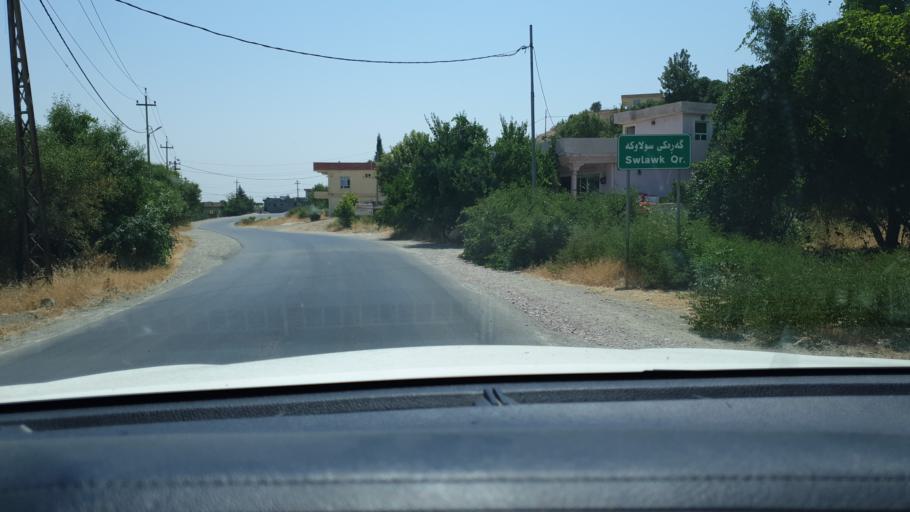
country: IQ
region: Arbil
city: Nahiyat Hiran
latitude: 36.2893
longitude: 44.4831
